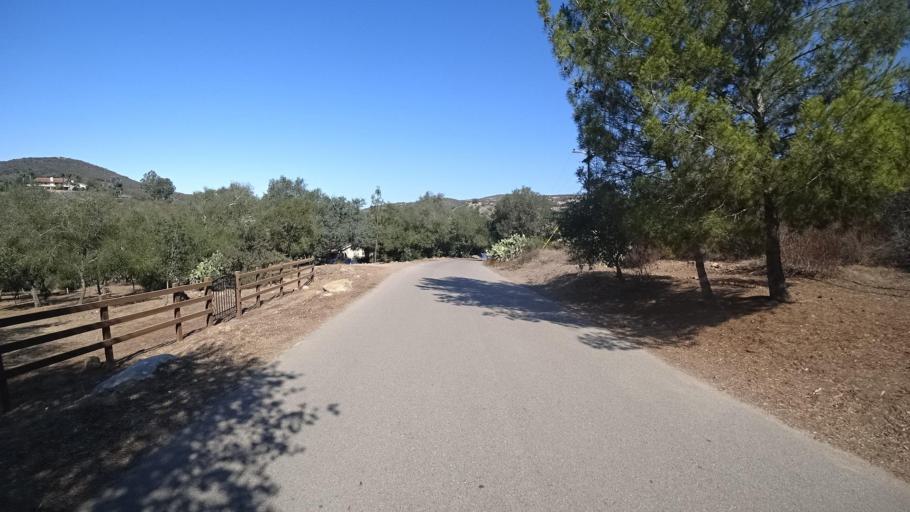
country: US
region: California
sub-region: San Diego County
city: Rancho Santa Fe
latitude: 33.0613
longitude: -117.1382
